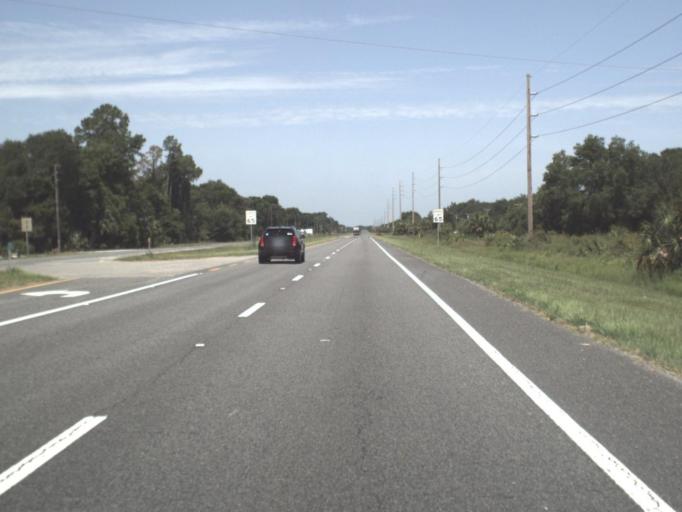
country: US
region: Florida
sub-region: Dixie County
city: Cross City
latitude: 29.6074
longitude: -83.0576
